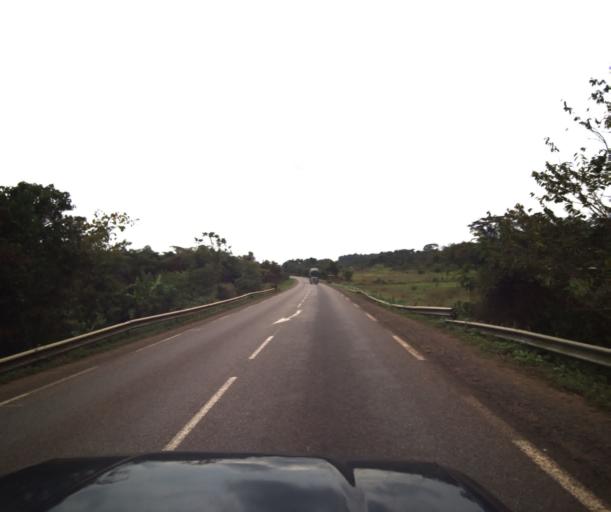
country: CM
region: Littoral
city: Edea
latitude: 3.8353
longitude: 10.4312
